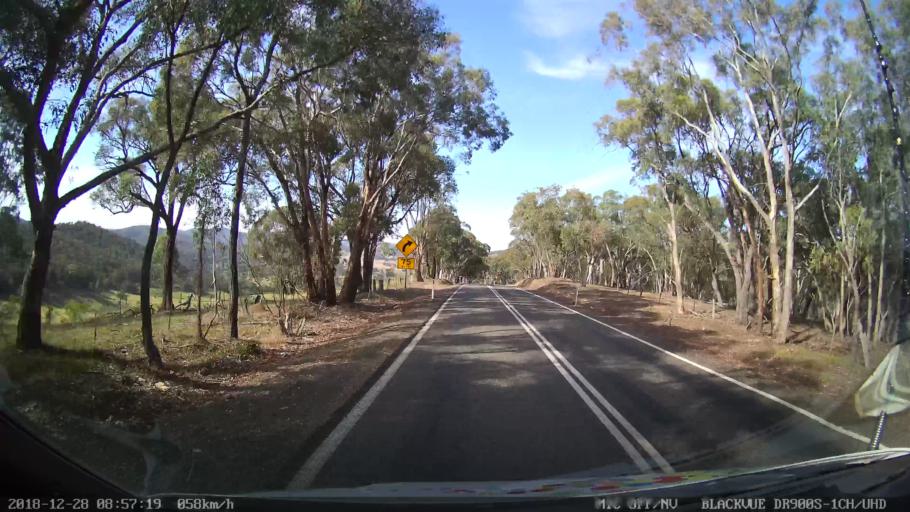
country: AU
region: New South Wales
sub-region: Upper Lachlan Shire
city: Crookwell
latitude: -34.1178
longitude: 149.3361
